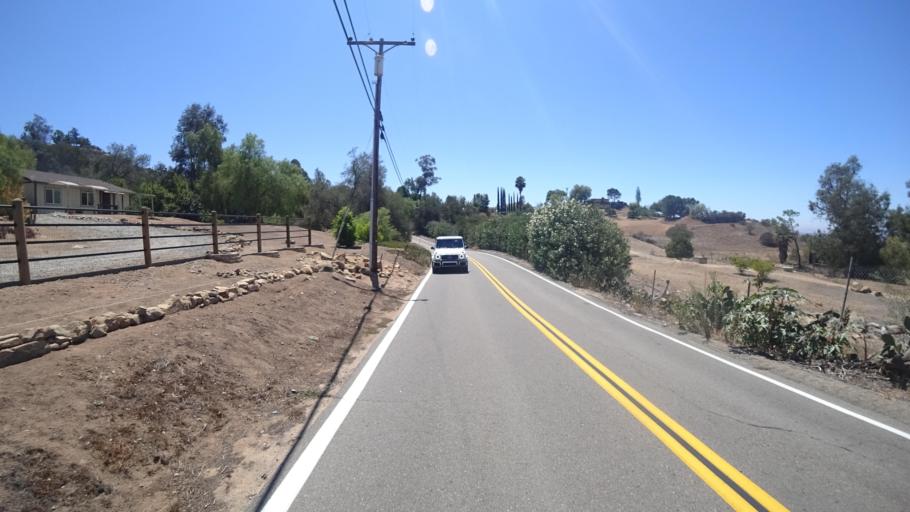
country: US
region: California
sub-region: San Diego County
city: Rainbow
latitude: 33.4018
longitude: -117.1383
